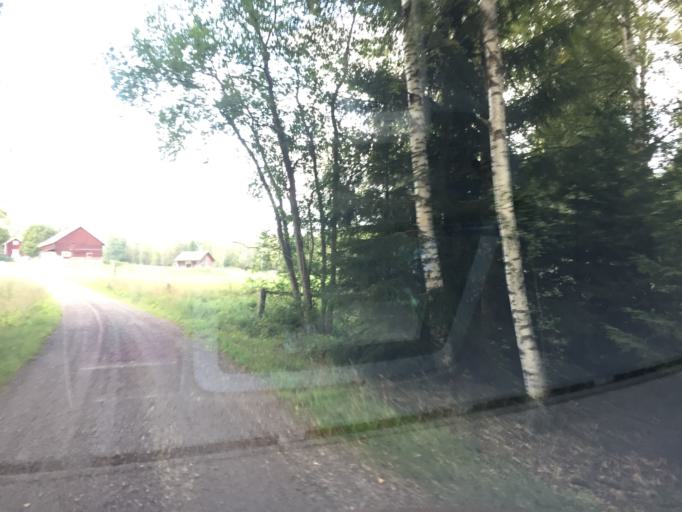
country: SE
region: Soedermanland
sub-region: Vingakers Kommun
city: Vingaker
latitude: 58.9858
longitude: 15.6953
